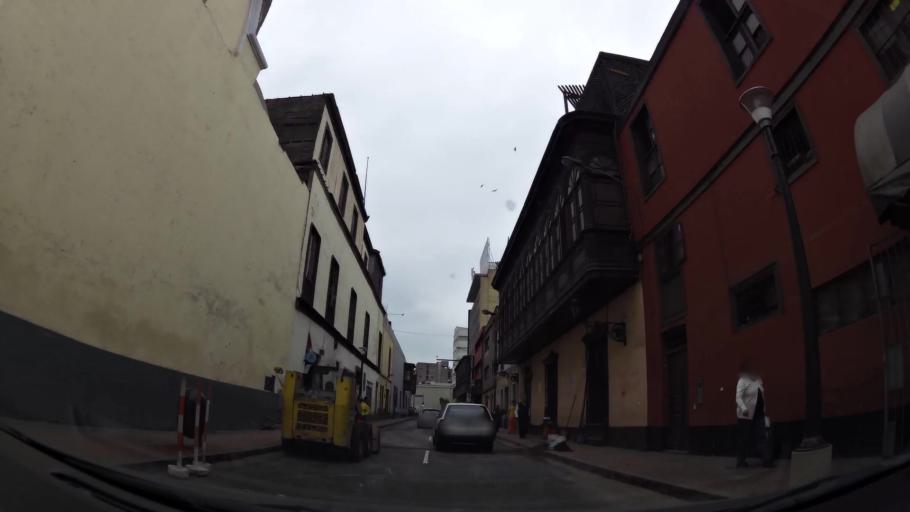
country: PE
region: Lima
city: Lima
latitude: -12.0461
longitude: -77.0270
